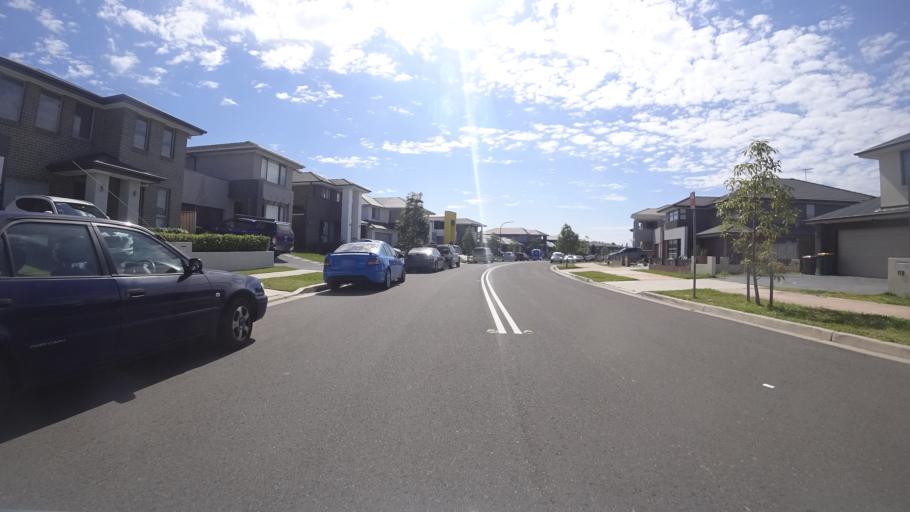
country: AU
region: New South Wales
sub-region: Bankstown
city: Milperra
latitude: -33.9332
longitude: 150.9606
